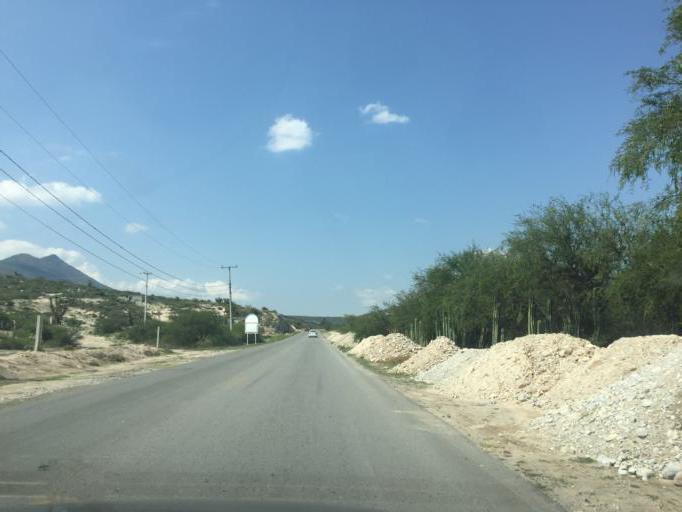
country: MX
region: Hidalgo
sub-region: Cardonal
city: Pozuelos
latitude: 20.5954
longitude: -99.1188
